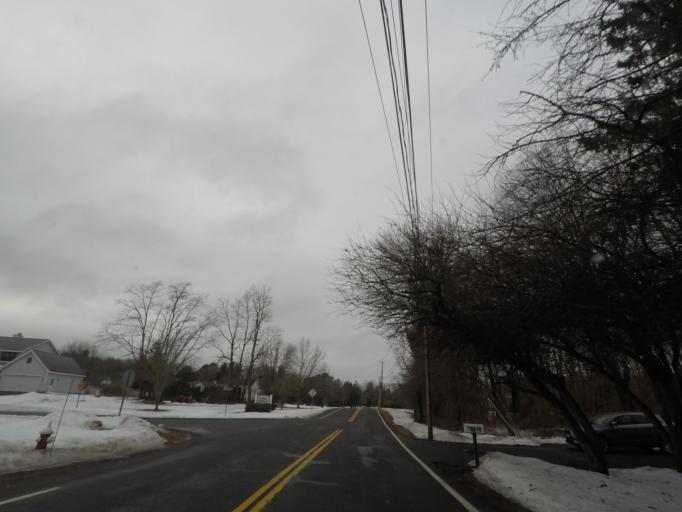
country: US
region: New York
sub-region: Schenectady County
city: Rotterdam
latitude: 42.7491
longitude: -73.9583
